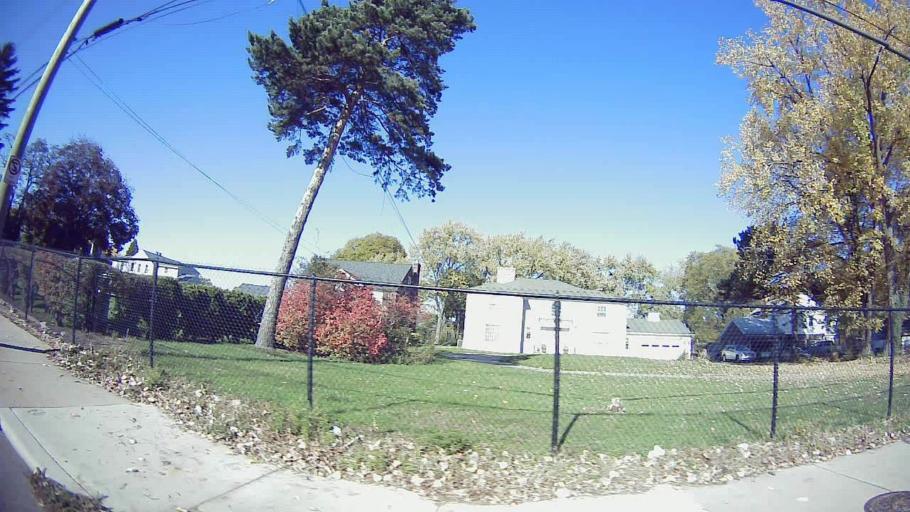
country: US
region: Michigan
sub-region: Wayne County
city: Highland Park
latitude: 42.4175
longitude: -83.1224
